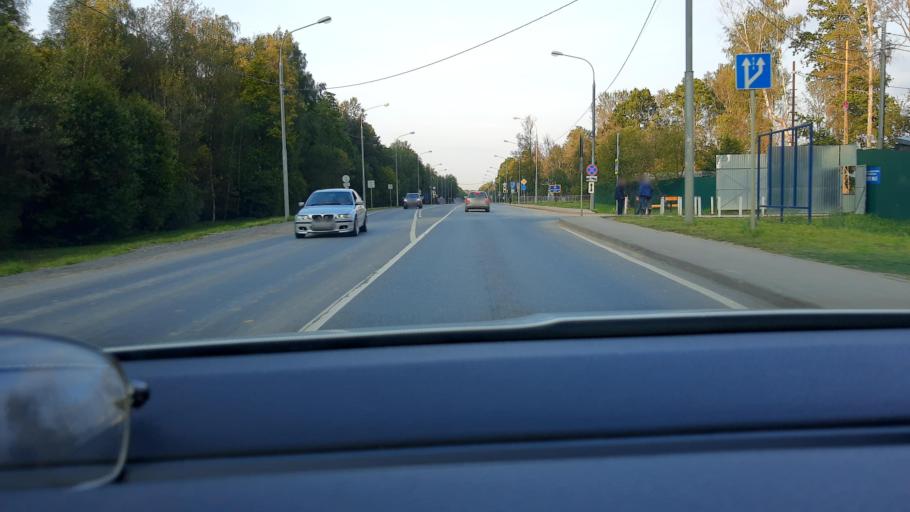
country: RU
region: Moskovskaya
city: Troitsk
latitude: 55.2922
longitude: 37.1824
